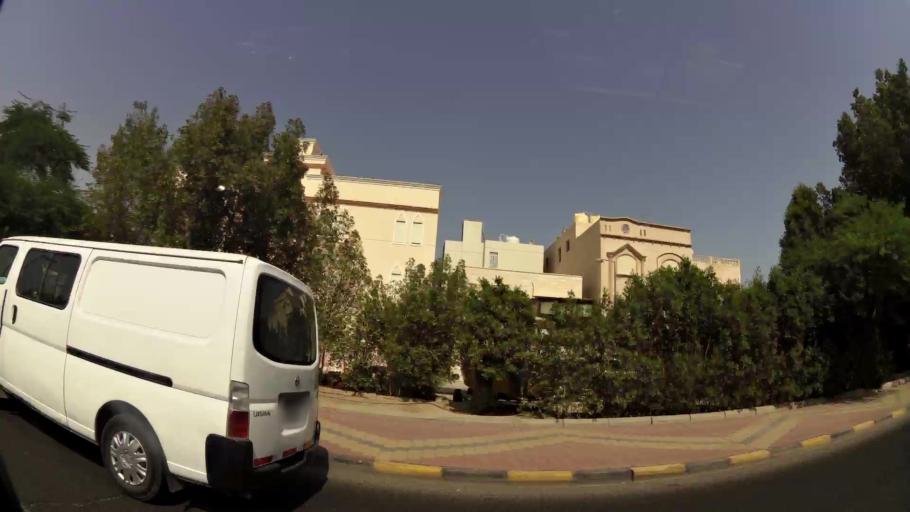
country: KW
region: Al Asimah
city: Ash Shamiyah
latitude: 29.3324
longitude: 47.9647
